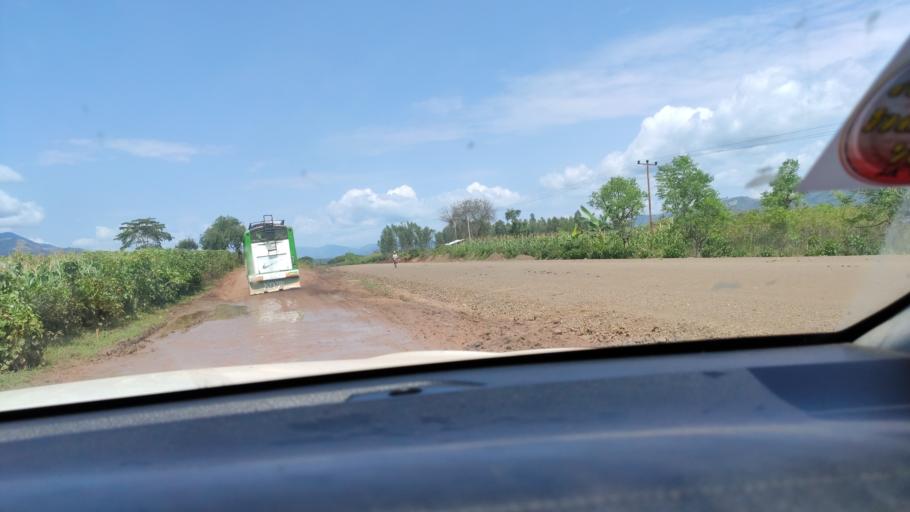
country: ET
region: Southern Nations, Nationalities, and People's Region
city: Felege Neway
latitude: 6.3672
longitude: 36.9929
